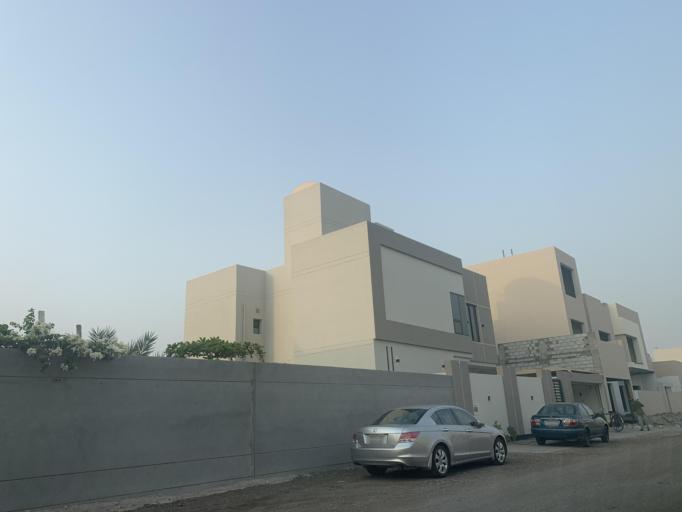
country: BH
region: Manama
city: Jidd Hafs
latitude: 26.2202
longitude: 50.5178
